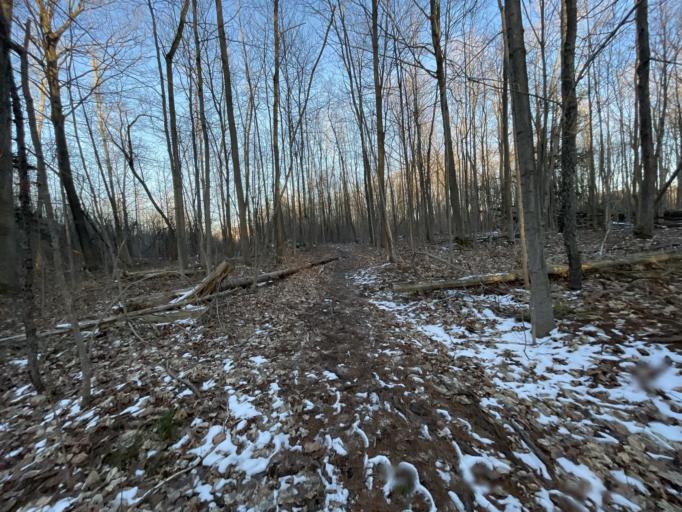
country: CA
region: Ontario
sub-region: Wellington County
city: Guelph
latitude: 43.5249
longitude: -80.3054
